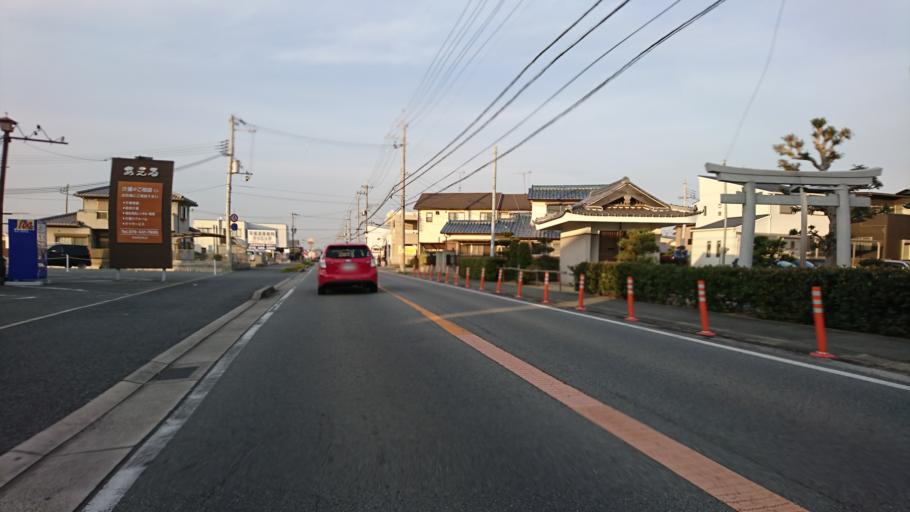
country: JP
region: Hyogo
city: Kakogawacho-honmachi
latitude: 34.7594
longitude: 134.8749
